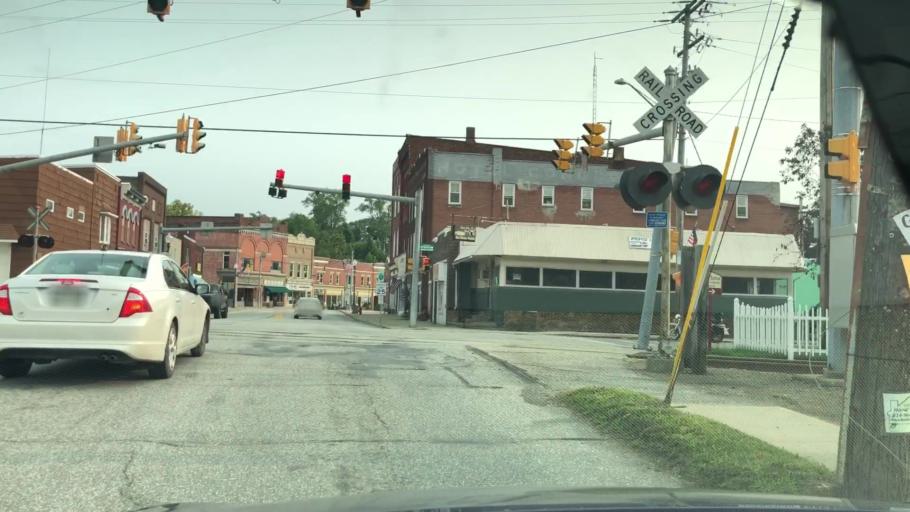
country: US
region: Pennsylvania
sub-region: Erie County
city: Union City
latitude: 41.8998
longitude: -79.8454
